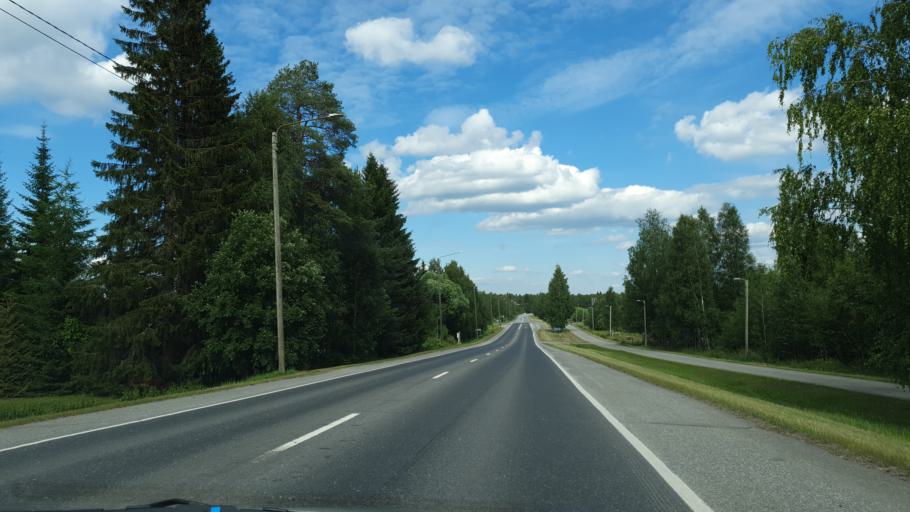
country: FI
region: Kainuu
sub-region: Kajaani
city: Kajaani
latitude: 64.2426
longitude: 27.7573
